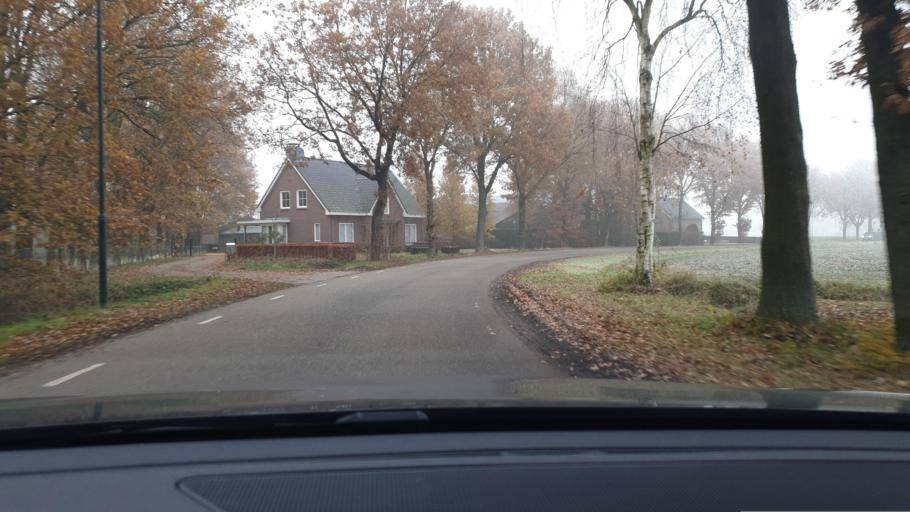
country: NL
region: North Brabant
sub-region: Gemeente Bladel en Netersel
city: Bladel
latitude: 51.3915
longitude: 5.1873
